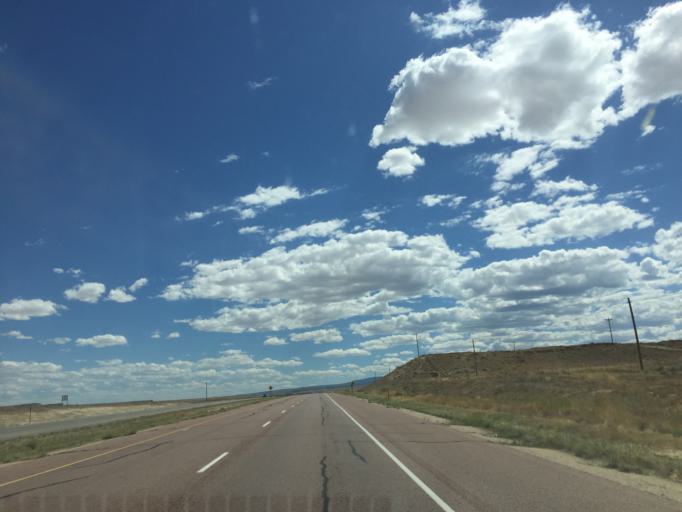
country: US
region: New Mexico
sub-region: McKinley County
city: Navajo
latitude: 36.2639
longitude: -108.7064
